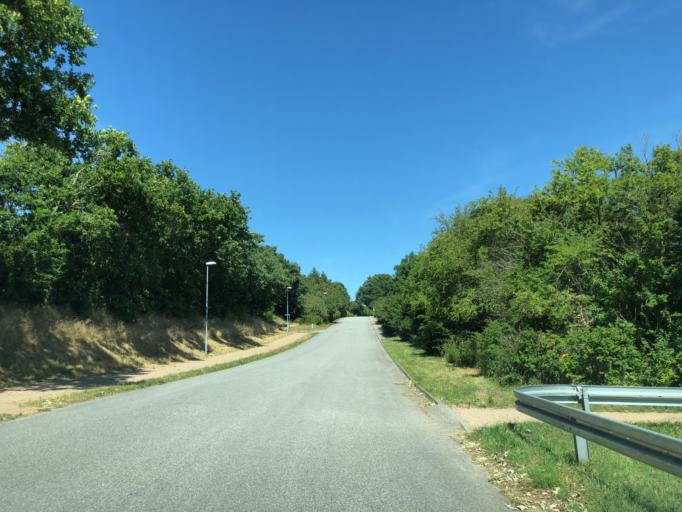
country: DK
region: Central Jutland
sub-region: Skive Kommune
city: Skive
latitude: 56.5469
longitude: 9.0123
